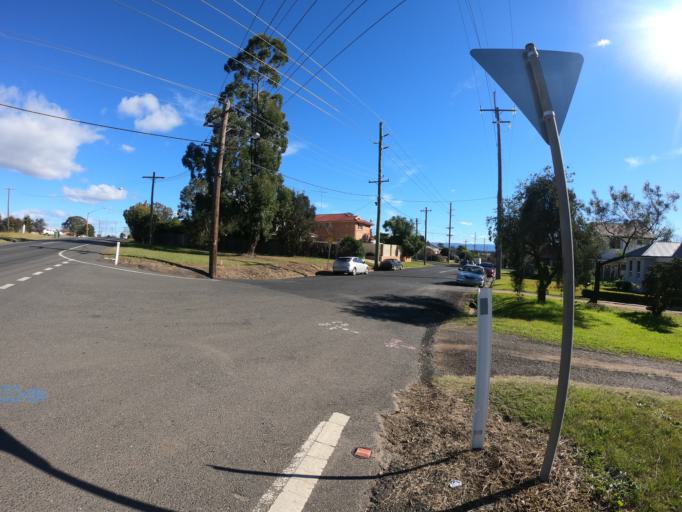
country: AU
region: New South Wales
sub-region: Hawkesbury
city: South Windsor
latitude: -33.6240
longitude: 150.8012
